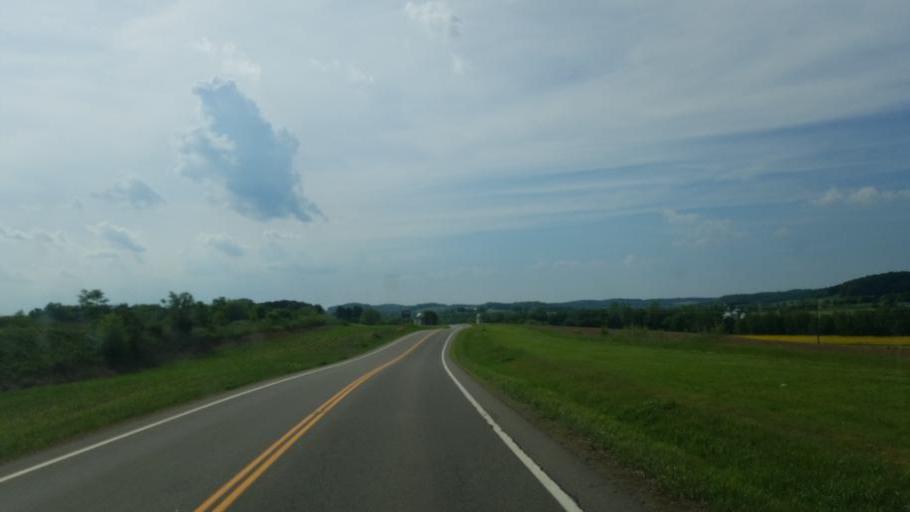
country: US
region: Ohio
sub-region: Ashland County
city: Loudonville
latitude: 40.6503
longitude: -82.2538
